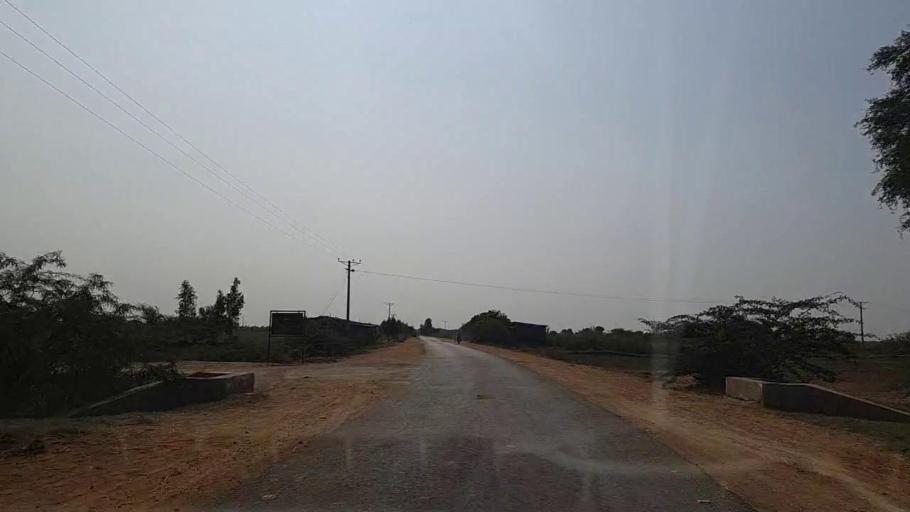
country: PK
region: Sindh
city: Chuhar Jamali
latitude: 24.3210
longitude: 67.9411
